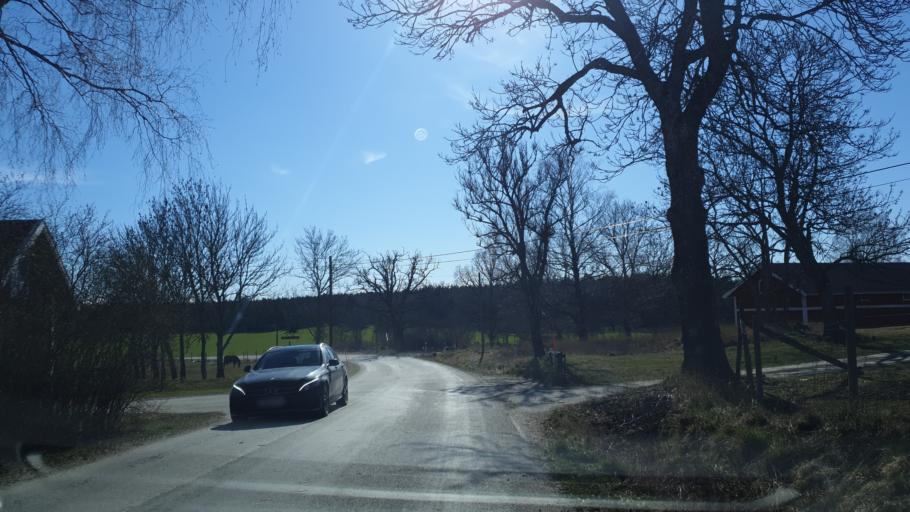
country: SE
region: Uppsala
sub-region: Enkopings Kommun
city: Dalby
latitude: 59.5571
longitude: 17.3149
